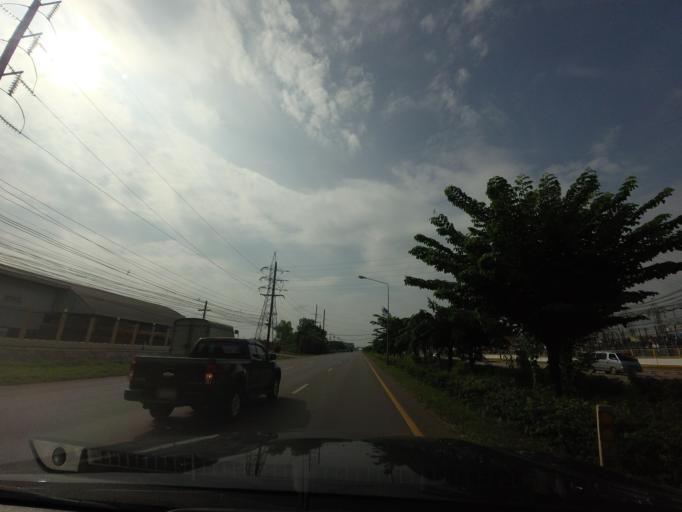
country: TH
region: Nong Khai
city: Nong Khai
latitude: 17.8217
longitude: 102.7573
